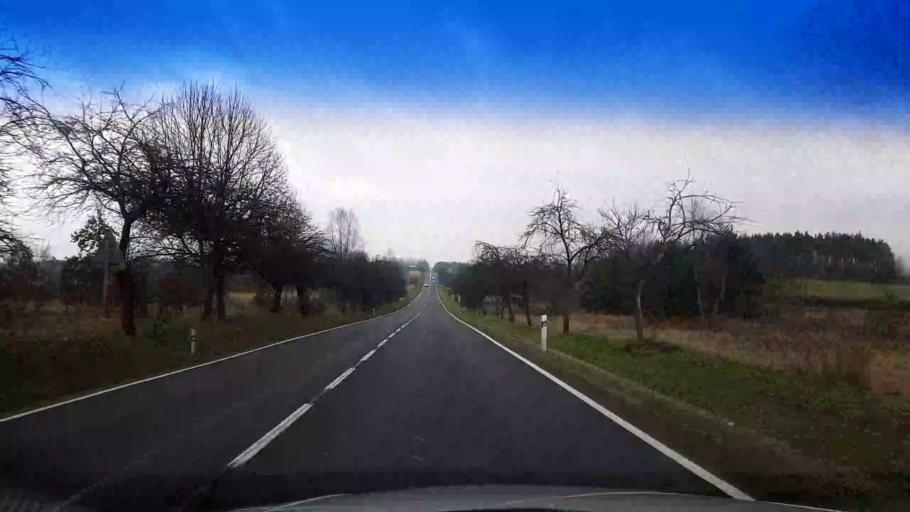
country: CZ
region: Karlovarsky
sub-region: Okres Cheb
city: Frantiskovy Lazne
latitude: 50.1372
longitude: 12.3228
